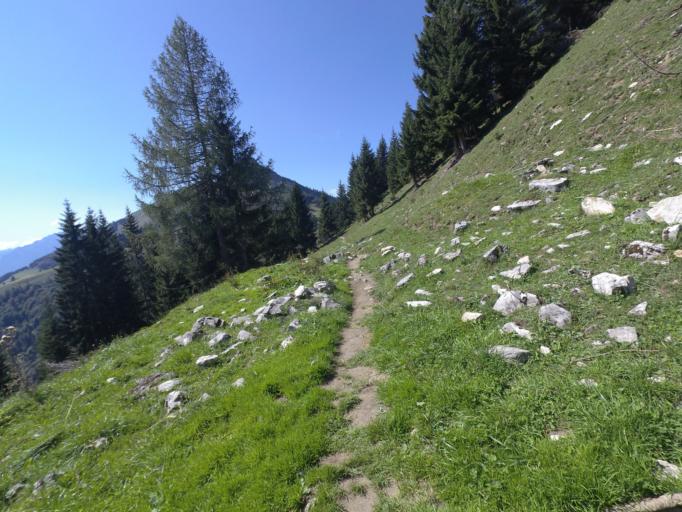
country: AT
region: Salzburg
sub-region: Politischer Bezirk Salzburg-Umgebung
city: Hintersee
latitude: 47.6877
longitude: 13.2614
